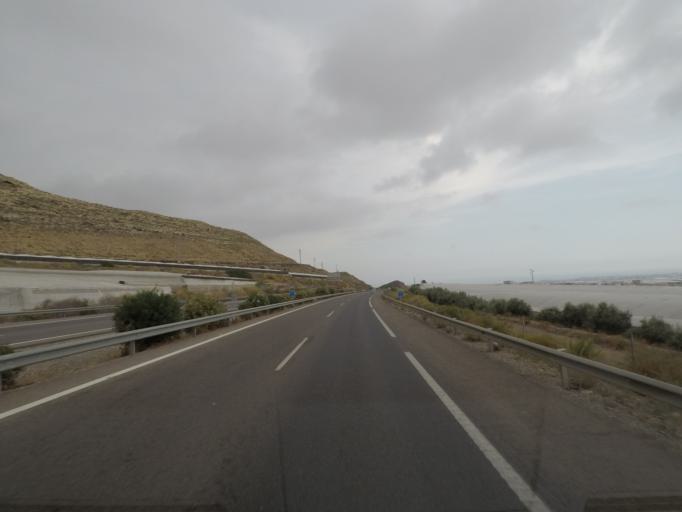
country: ES
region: Andalusia
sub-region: Provincia de Almeria
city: Vicar
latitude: 36.8133
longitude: -2.6428
